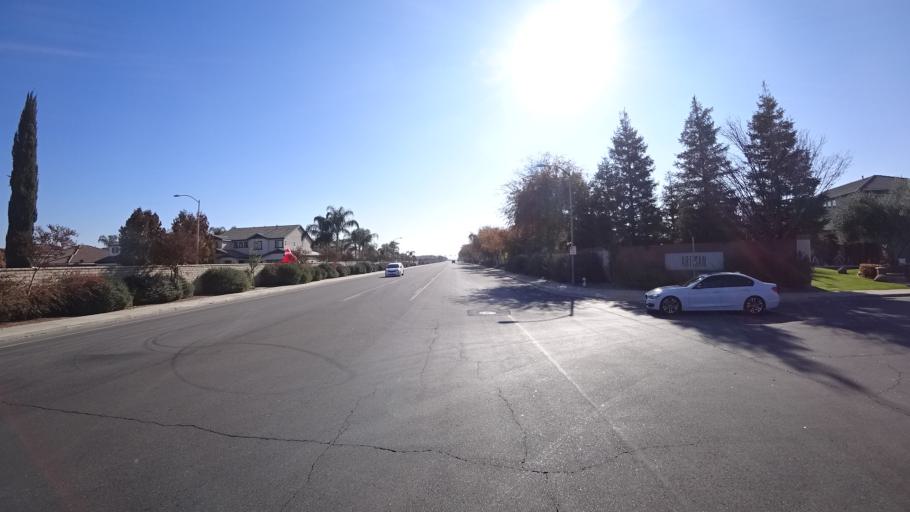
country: US
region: California
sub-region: Kern County
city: Greenacres
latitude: 35.3068
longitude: -119.1188
